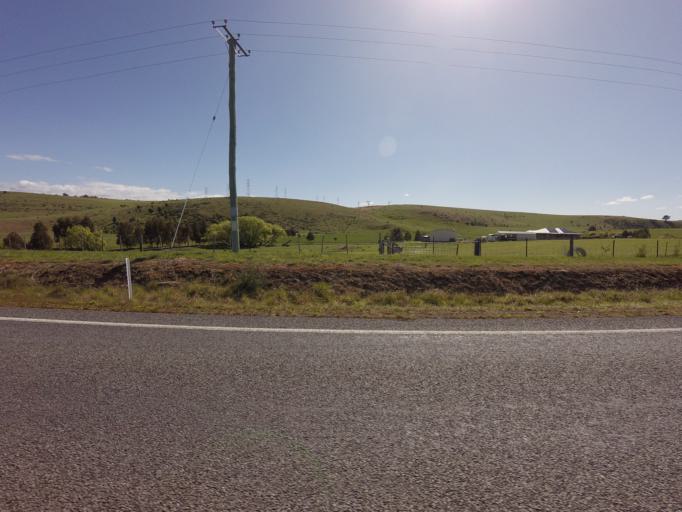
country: AU
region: Tasmania
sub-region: Derwent Valley
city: New Norfolk
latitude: -42.6609
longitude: 146.9352
